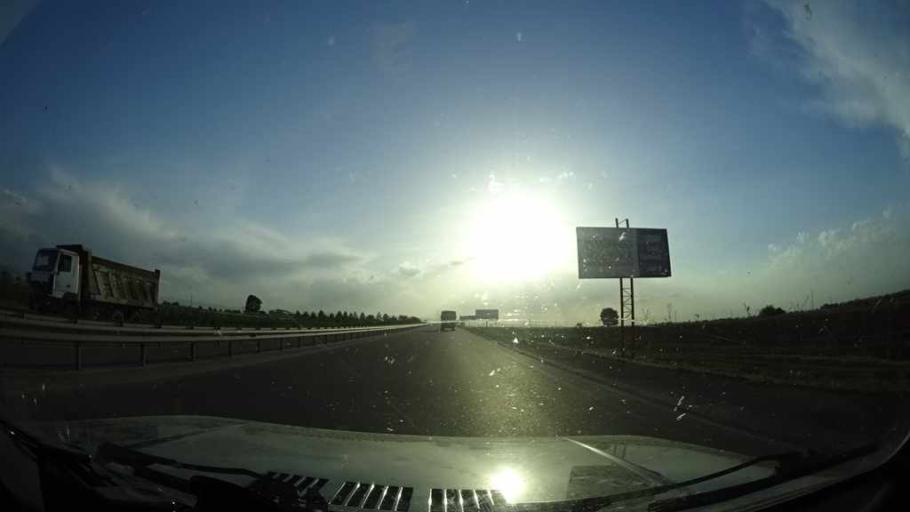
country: AZ
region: Samux
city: Samux
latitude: 40.6898
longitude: 46.4994
